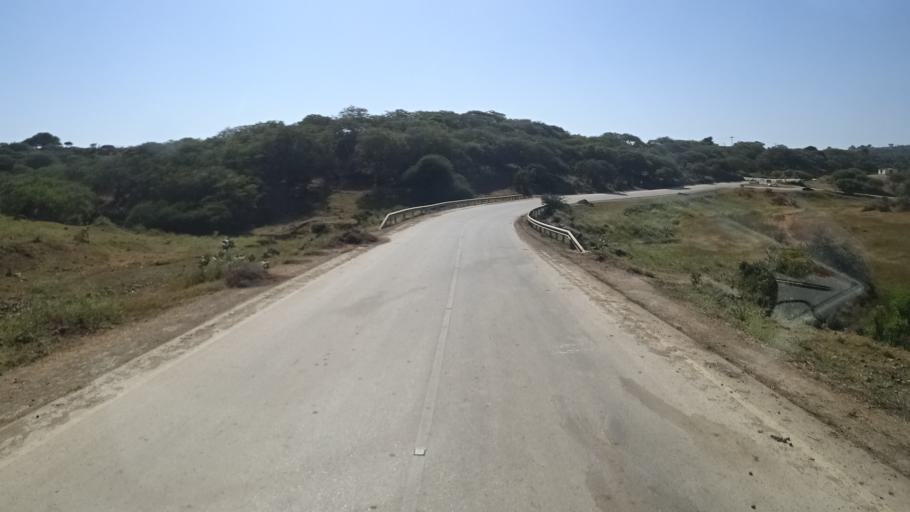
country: OM
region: Zufar
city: Salalah
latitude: 17.0660
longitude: 54.5999
